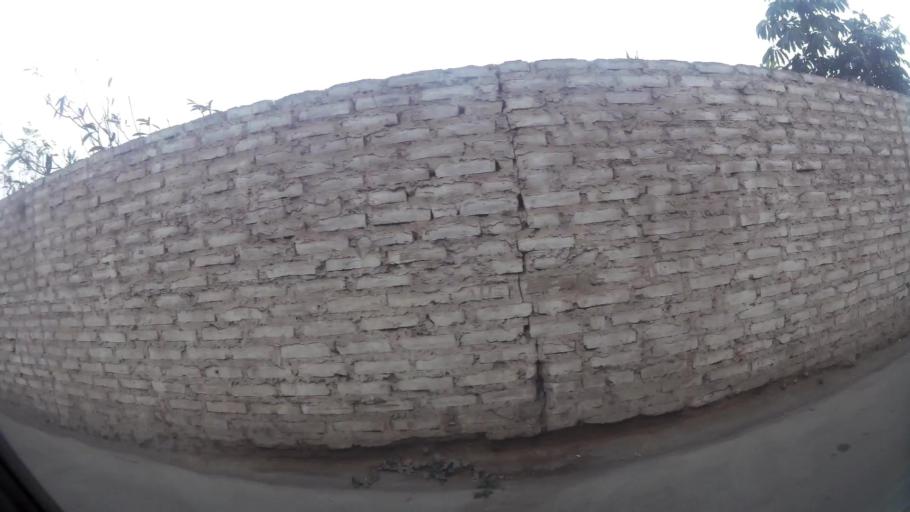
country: PE
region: Lima
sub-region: Provincia de Huaral
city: Chancay
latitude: -11.5596
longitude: -77.2730
